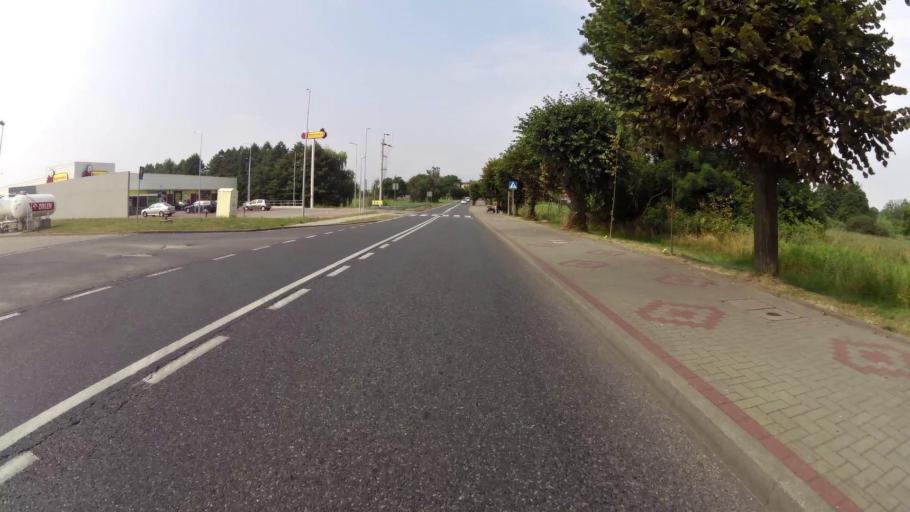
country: PL
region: West Pomeranian Voivodeship
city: Trzcinsko Zdroj
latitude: 52.9617
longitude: 14.6155
